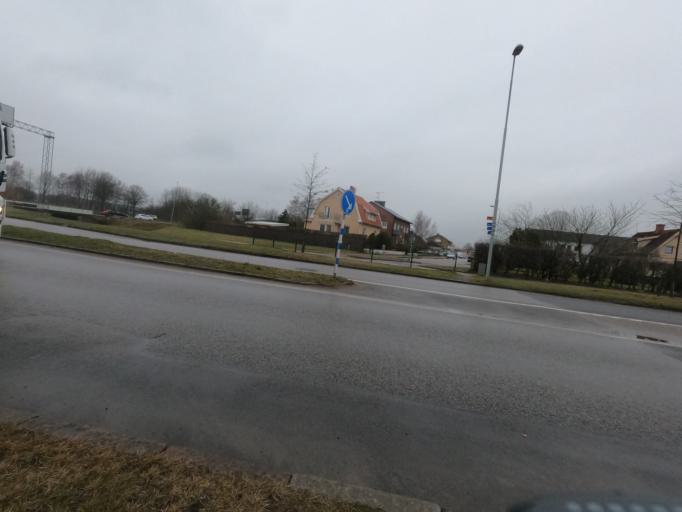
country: SE
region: Halland
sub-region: Halmstads Kommun
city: Halmstad
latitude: 56.6726
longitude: 12.8822
